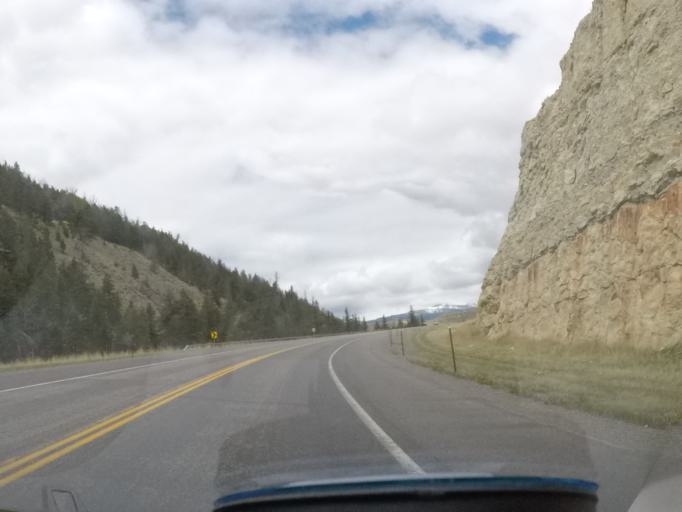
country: US
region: Wyoming
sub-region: Sublette County
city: Pinedale
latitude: 43.5790
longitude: -109.7613
